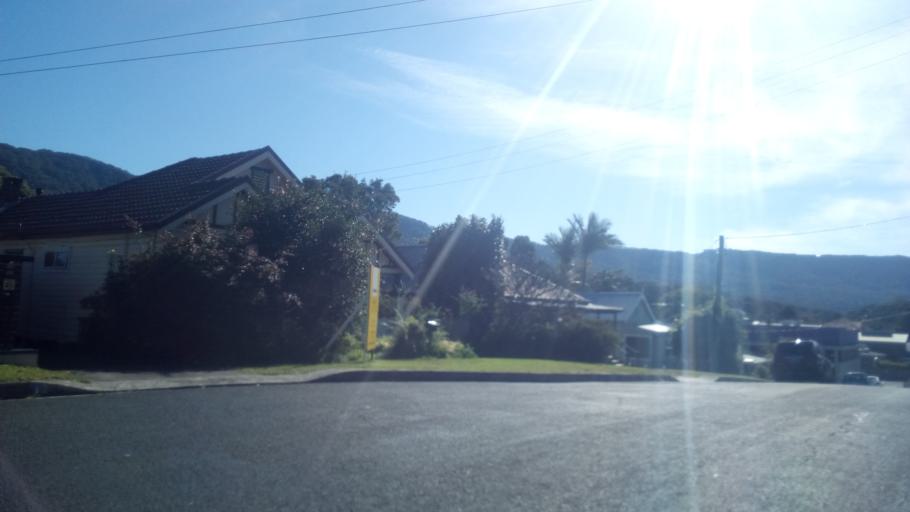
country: AU
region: New South Wales
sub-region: Wollongong
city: Bulli
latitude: -34.3405
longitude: 150.9093
